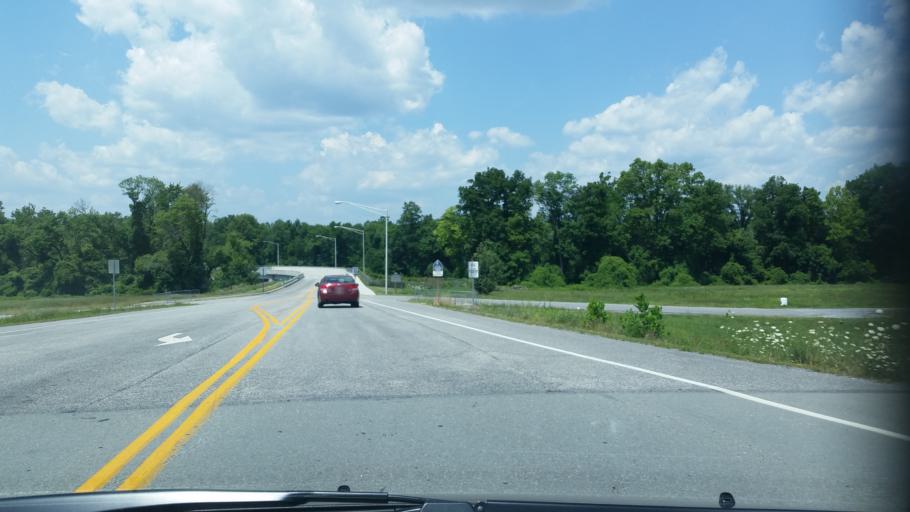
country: US
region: Pennsylvania
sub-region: Dauphin County
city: Hershey
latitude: 40.2859
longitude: -76.6760
